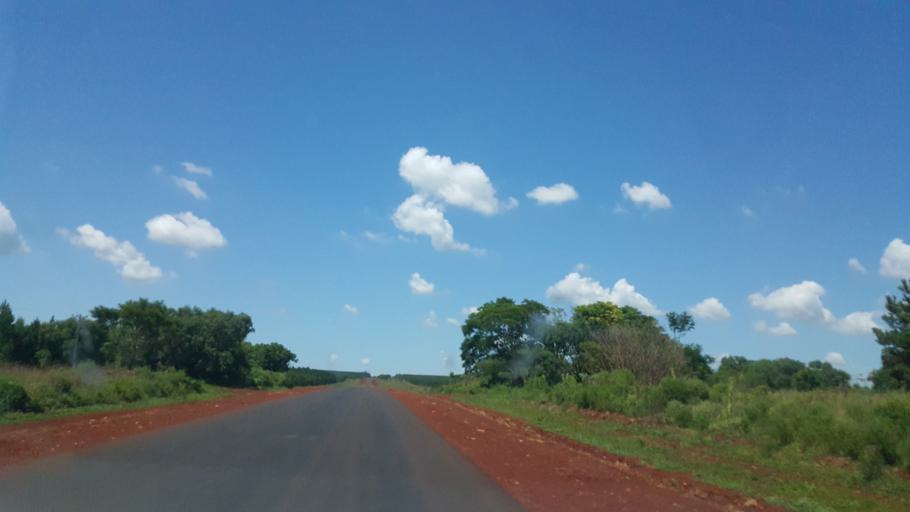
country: AR
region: Corrientes
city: Santo Tome
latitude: -28.4808
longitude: -56.0364
